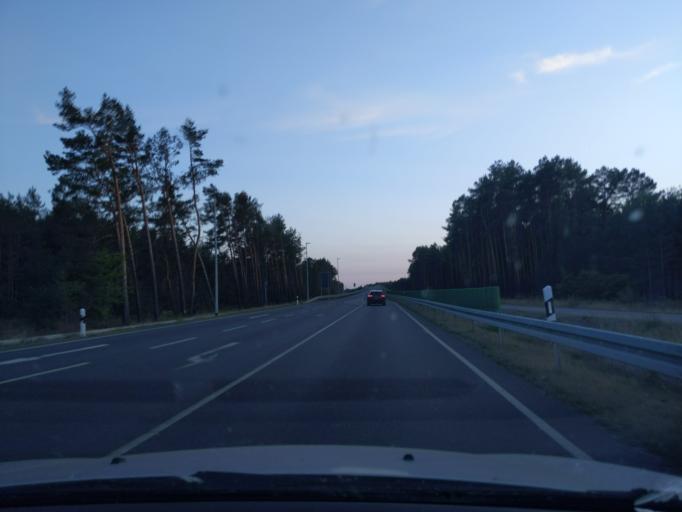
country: DE
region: Saxony
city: Hoyerswerda
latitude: 51.4282
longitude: 14.3003
